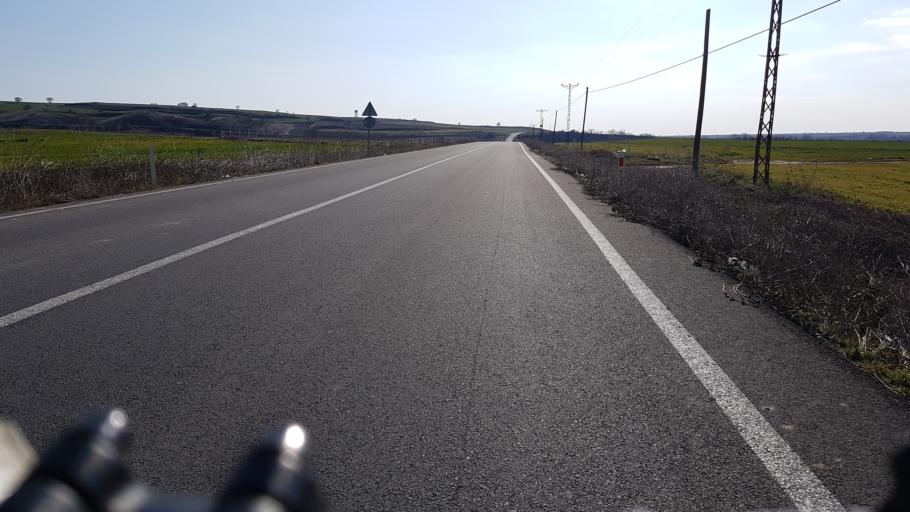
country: TR
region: Tekirdag
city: Saray
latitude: 41.3619
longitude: 27.8555
